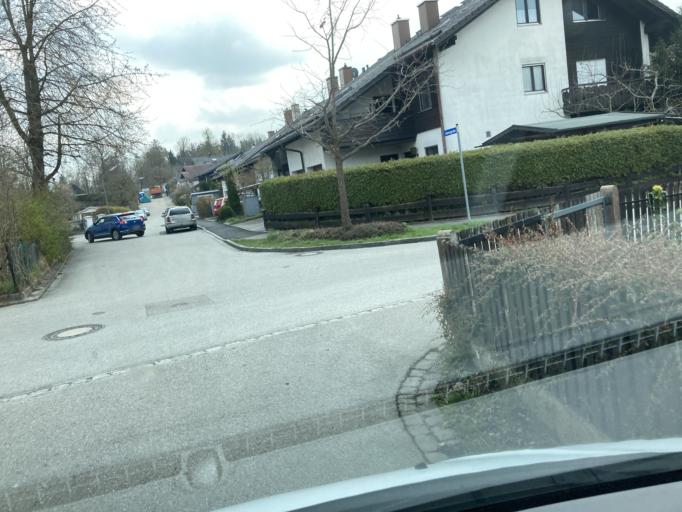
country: DE
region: Bavaria
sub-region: Upper Bavaria
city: Grafing bei Munchen
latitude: 48.0406
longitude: 11.9622
